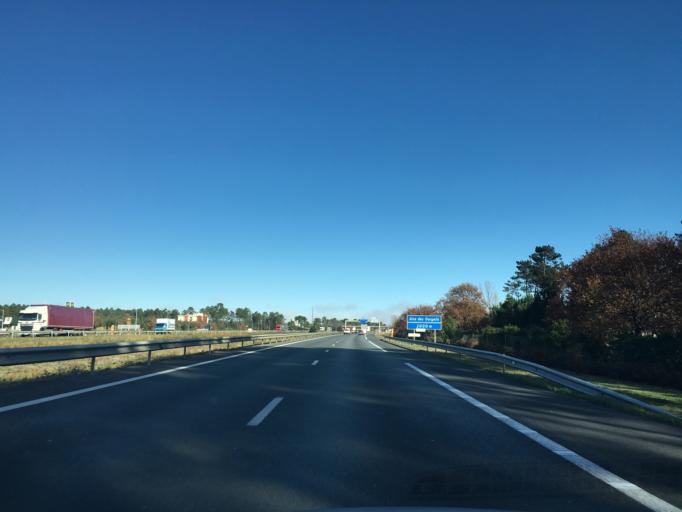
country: FR
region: Aquitaine
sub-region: Departement de la Gironde
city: Marcheprime
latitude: 44.6562
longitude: -0.8300
